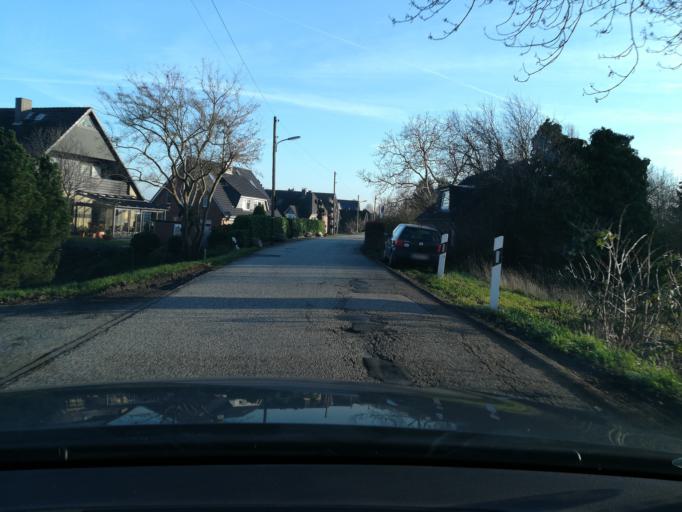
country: DE
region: Lower Saxony
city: Stelle
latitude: 53.4495
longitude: 10.1009
